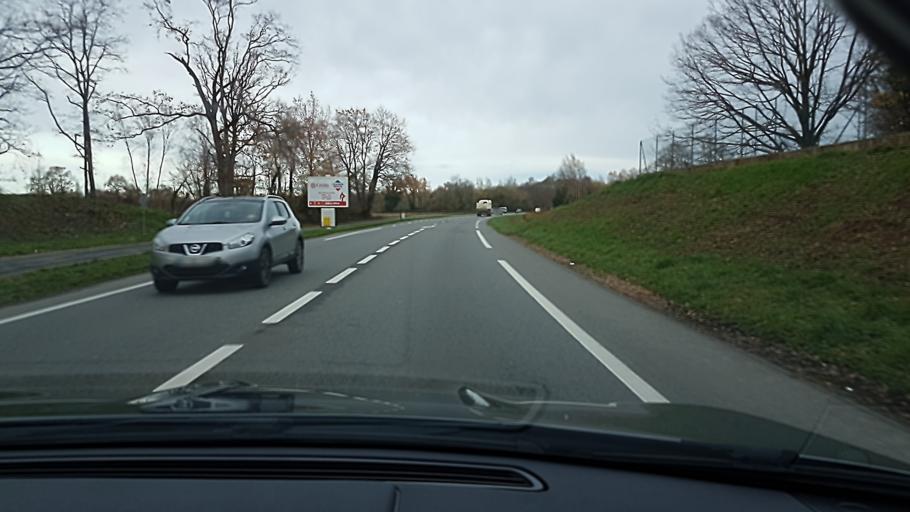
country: FR
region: Aquitaine
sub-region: Departement des Pyrenees-Atlantiques
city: Idron
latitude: 43.3030
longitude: -0.3084
